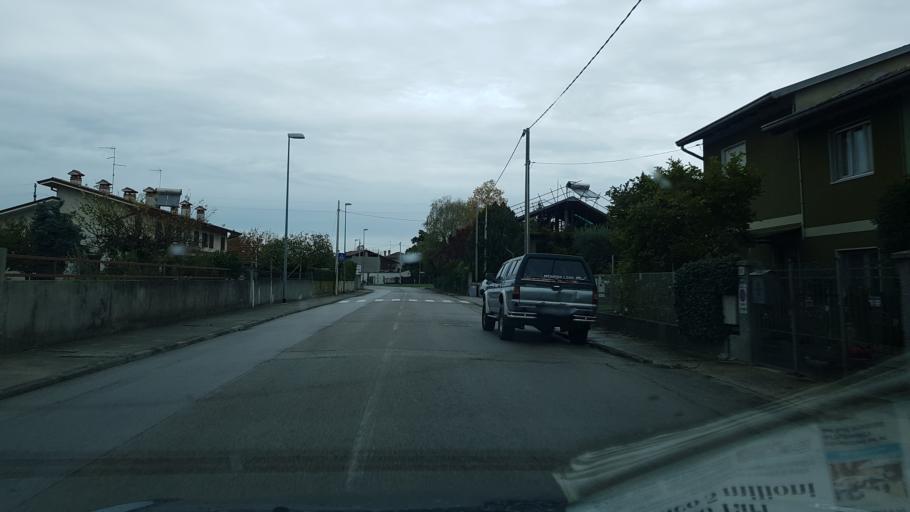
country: IT
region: Friuli Venezia Giulia
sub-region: Provincia di Udine
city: San Valentino
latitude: 45.7923
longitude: 13.4146
